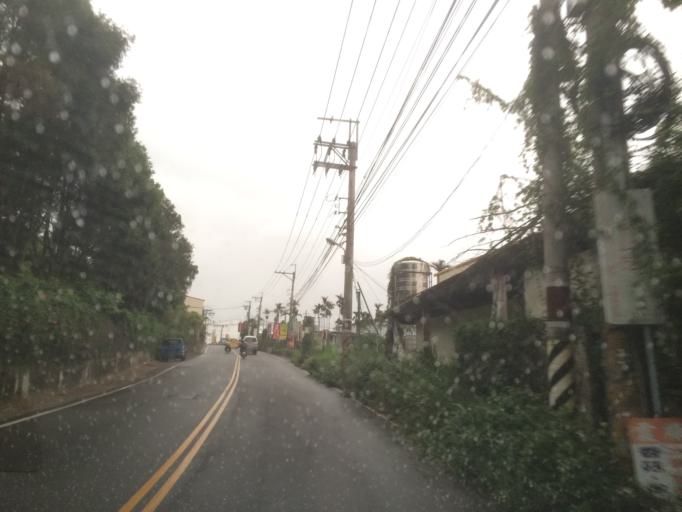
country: TW
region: Taiwan
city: Fengyuan
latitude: 24.1884
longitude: 120.8137
